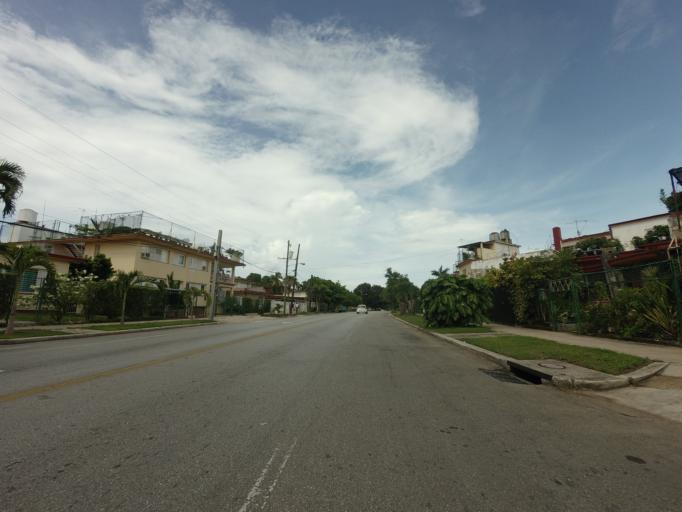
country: CU
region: La Habana
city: Havana
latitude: 23.1123
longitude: -82.4307
